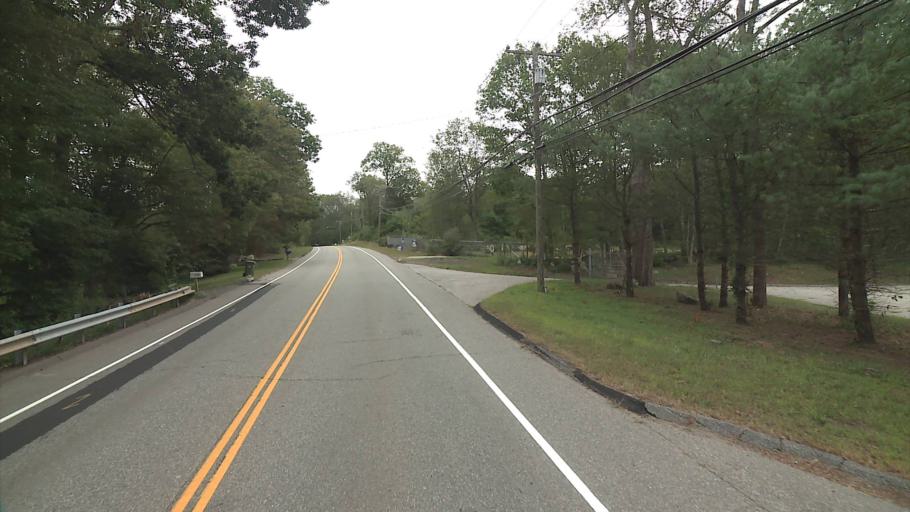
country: US
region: Connecticut
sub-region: Tolland County
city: Hebron
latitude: 41.6727
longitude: -72.3908
